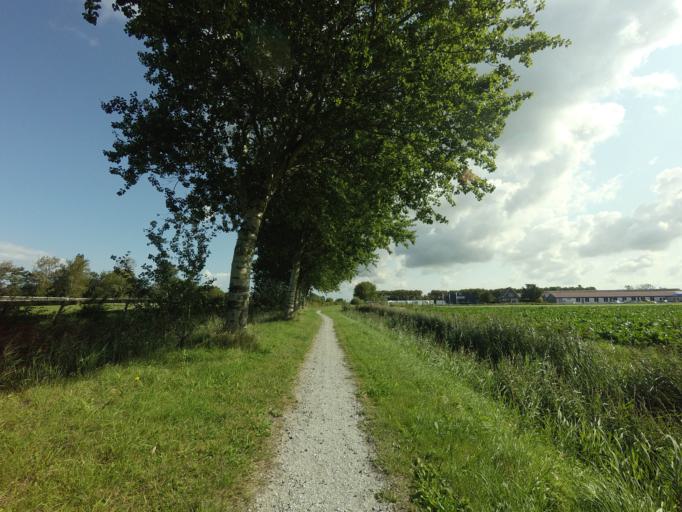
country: NL
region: Friesland
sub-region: Gemeente Franekeradeel
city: Tzummarum
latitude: 53.2403
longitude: 5.5406
